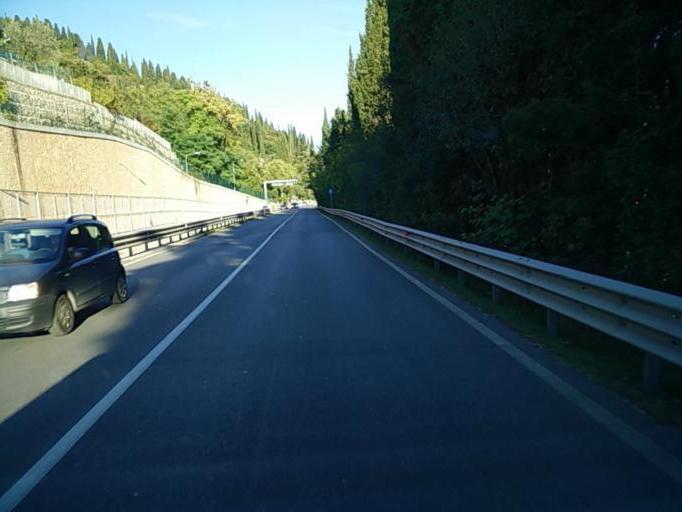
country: IT
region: Lombardy
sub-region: Provincia di Brescia
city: Salo
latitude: 45.6116
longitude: 10.5397
